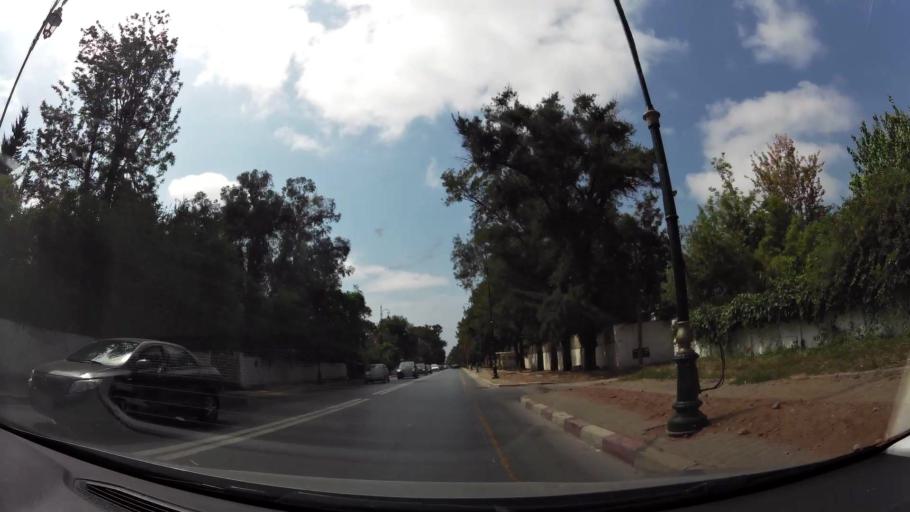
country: MA
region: Rabat-Sale-Zemmour-Zaer
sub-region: Rabat
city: Rabat
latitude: 33.9805
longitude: -6.8434
